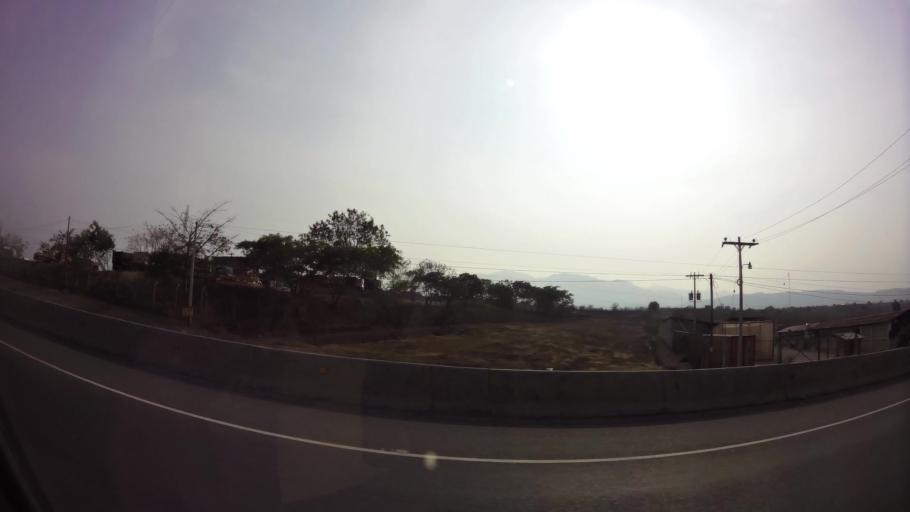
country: HN
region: Comayagua
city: Comayagua
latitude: 14.4186
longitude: -87.6261
